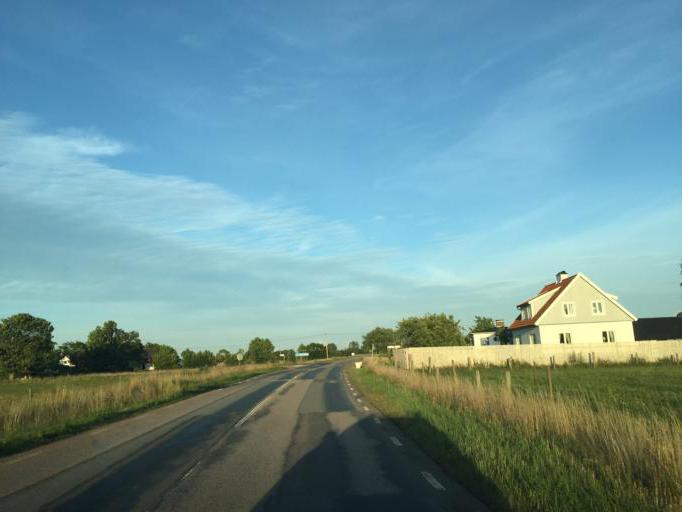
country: SE
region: Skane
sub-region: Angelholms Kommun
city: Vejbystrand
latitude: 56.3151
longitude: 12.7959
